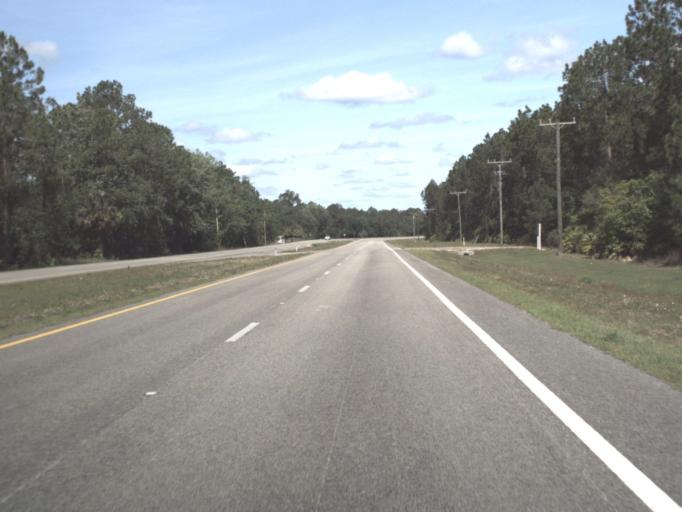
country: US
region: Florida
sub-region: Flagler County
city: Bunnell
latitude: 29.4301
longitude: -81.2274
